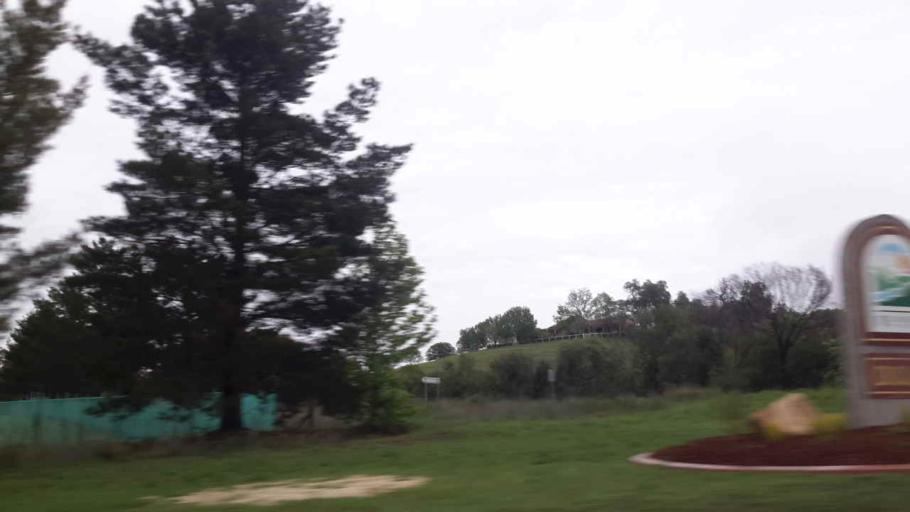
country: AU
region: New South Wales
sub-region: Wollondilly
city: Douglas Park
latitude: -34.1700
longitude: 150.7137
